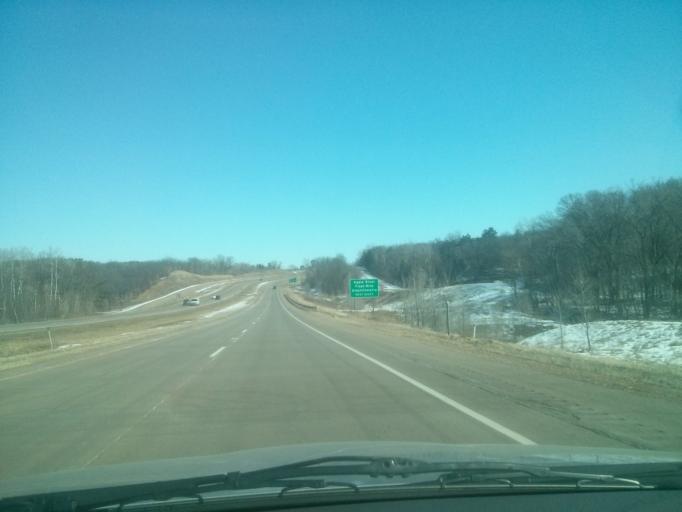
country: US
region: Wisconsin
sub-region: Saint Croix County
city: Somerset
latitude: 45.0994
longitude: -92.7328
